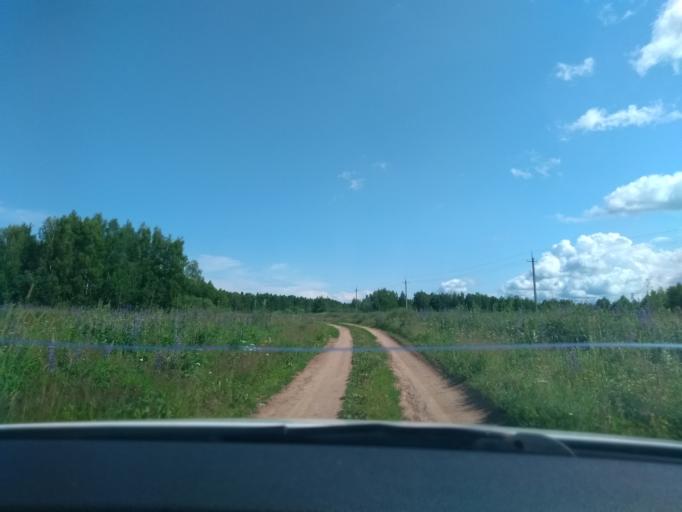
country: RU
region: Perm
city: Sylva
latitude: 57.8234
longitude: 56.7455
